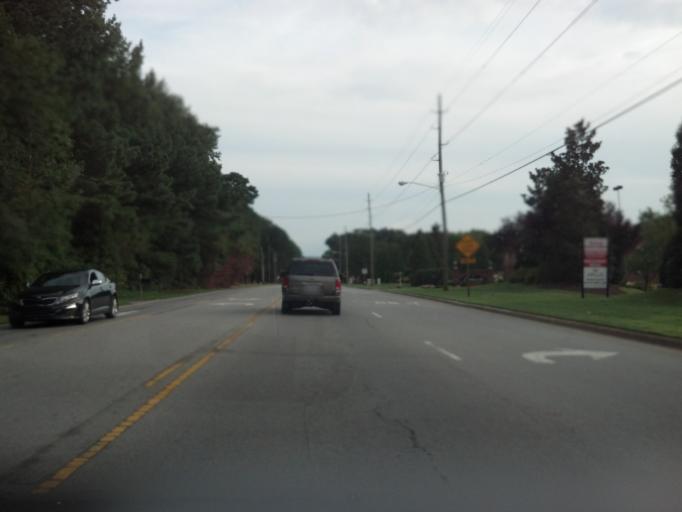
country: US
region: North Carolina
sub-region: Pitt County
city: Summerfield
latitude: 35.5735
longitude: -77.3825
